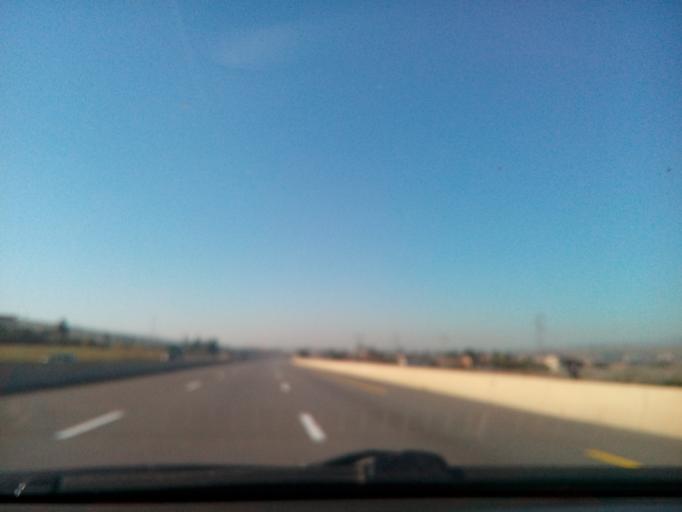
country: DZ
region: Chlef
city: Boukadir
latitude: 36.0354
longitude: 1.0813
